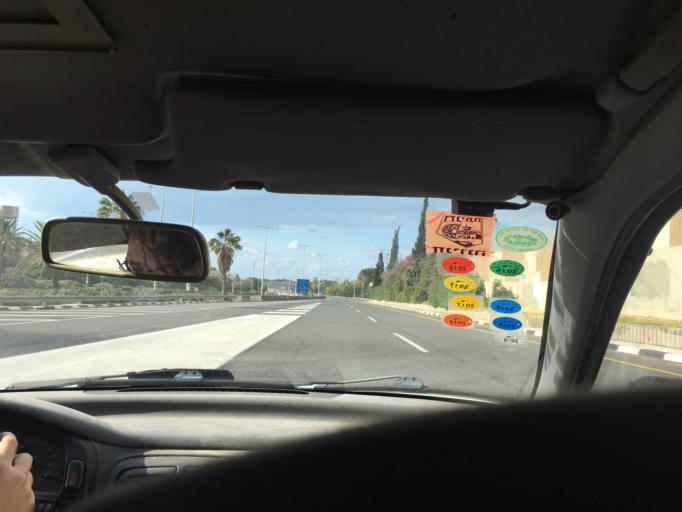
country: IL
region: Tel Aviv
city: Ramat HaSharon
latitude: 32.1359
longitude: 34.8321
